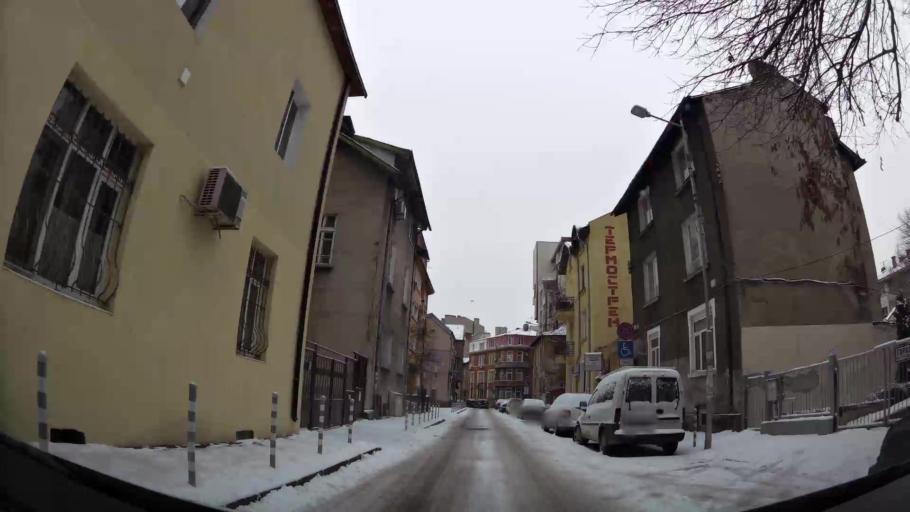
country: BG
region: Sofia-Capital
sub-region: Stolichna Obshtina
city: Sofia
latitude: 42.7038
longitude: 23.3316
